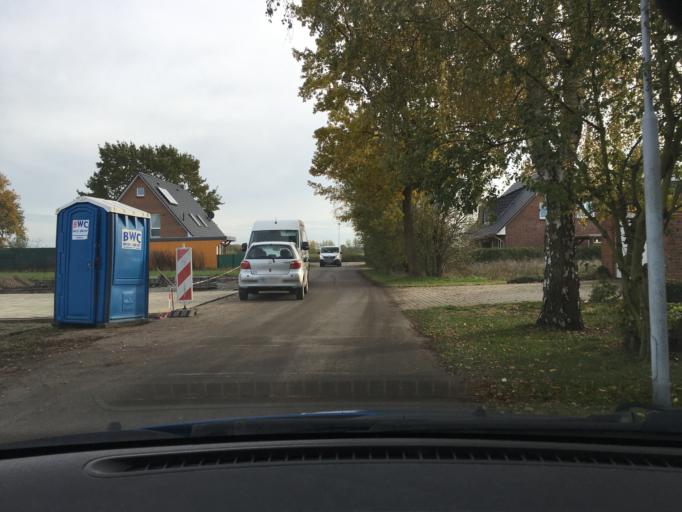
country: DE
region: Lower Saxony
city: Wittorf
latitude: 53.3242
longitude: 10.3666
